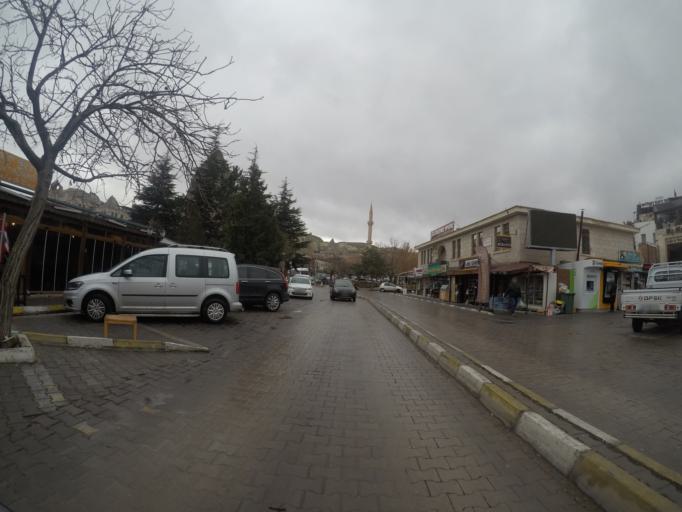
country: TR
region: Nevsehir
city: Goereme
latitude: 38.6430
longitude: 34.8292
